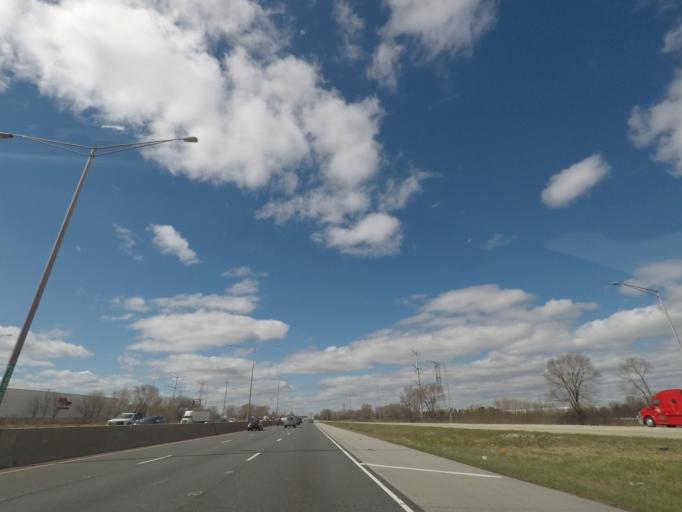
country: US
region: Illinois
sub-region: Will County
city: Romeoville
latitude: 41.6719
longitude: -88.0932
